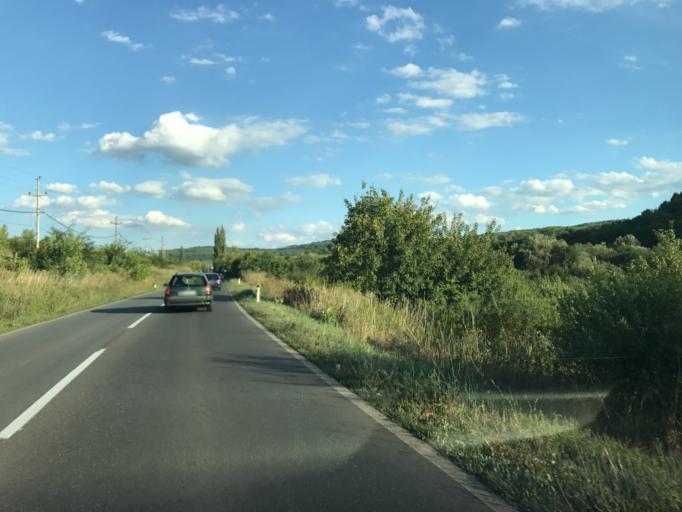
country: RS
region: Central Serbia
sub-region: Belgrade
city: Zvezdara
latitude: 44.7266
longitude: 20.6244
